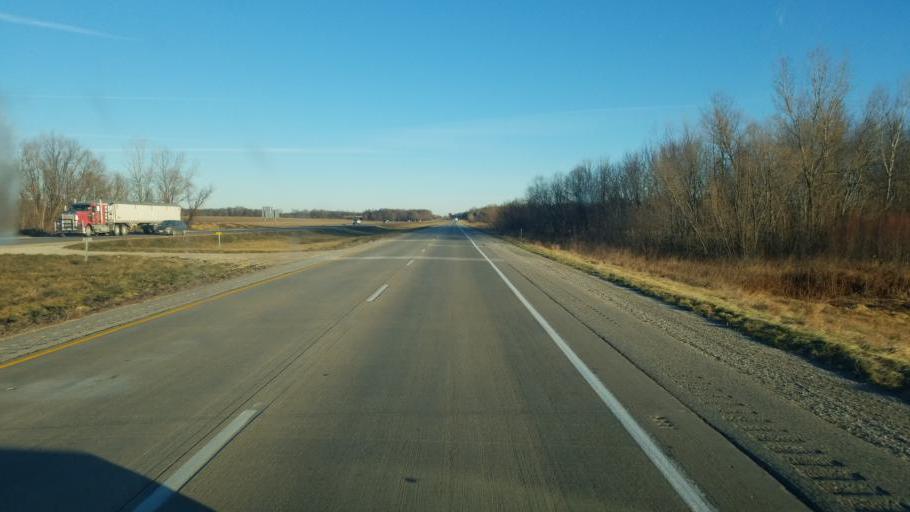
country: US
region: Iowa
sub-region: Wapello County
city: Eddyville
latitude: 41.1902
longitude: -92.6399
